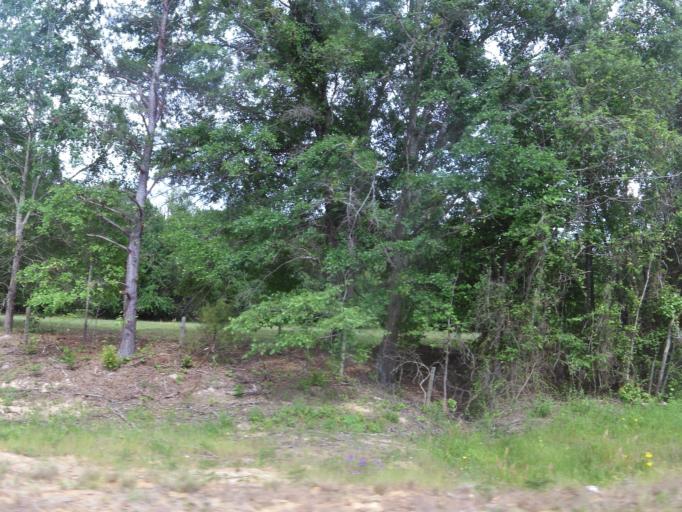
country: US
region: Georgia
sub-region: McDuffie County
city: Thomson
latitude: 33.3837
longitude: -82.4721
